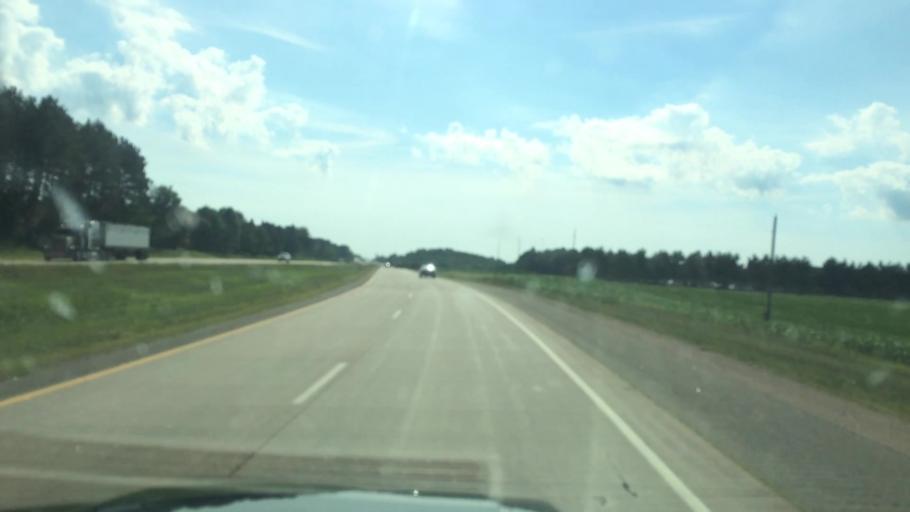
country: US
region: Wisconsin
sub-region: Shawano County
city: Wittenberg
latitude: 44.8037
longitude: -89.0292
